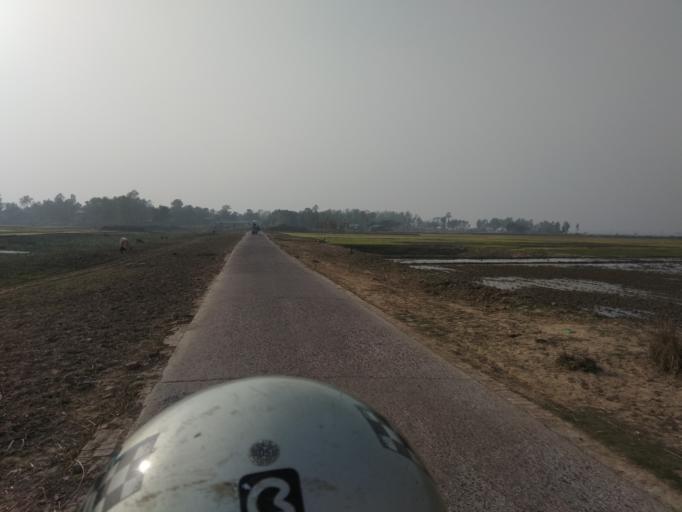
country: BD
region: Rajshahi
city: Ishurdi
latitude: 24.4884
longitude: 89.2065
